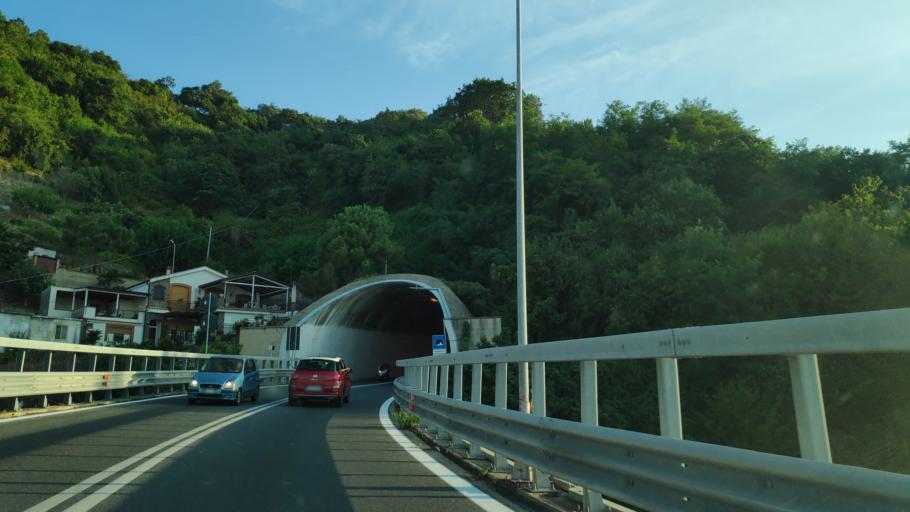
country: IT
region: Calabria
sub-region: Provincia di Reggio Calabria
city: Scilla
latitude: 38.2524
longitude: 15.7287
